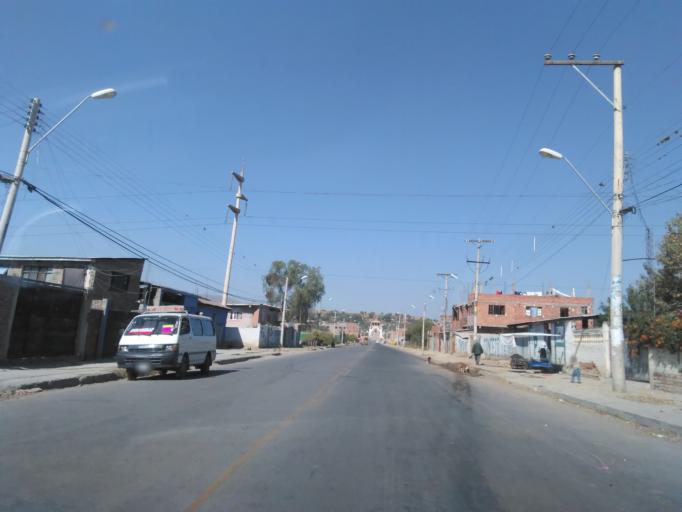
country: BO
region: Cochabamba
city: Sipe Sipe
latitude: -17.4141
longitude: -66.2829
